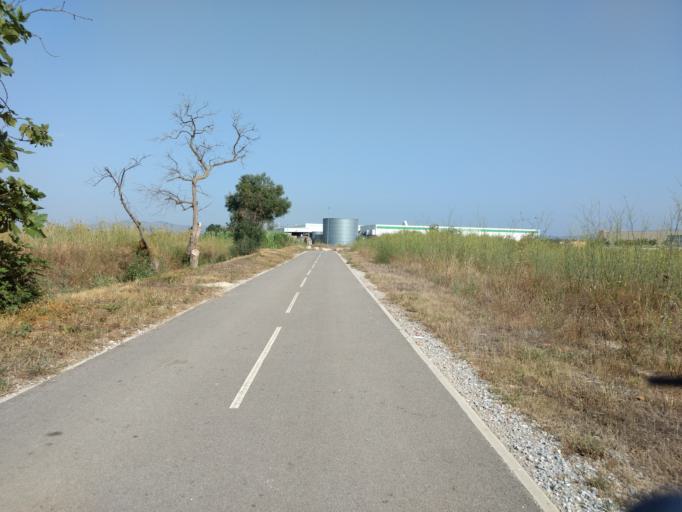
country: FR
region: Languedoc-Roussillon
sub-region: Departement des Pyrenees-Orientales
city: Pia
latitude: 42.7707
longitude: 2.9123
